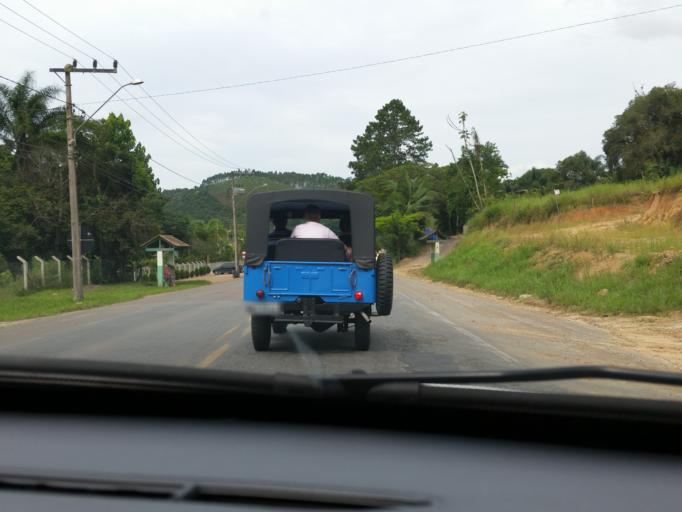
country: BR
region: Santa Catarina
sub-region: Rodeio
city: Gavea
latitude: -27.0270
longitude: -49.3790
